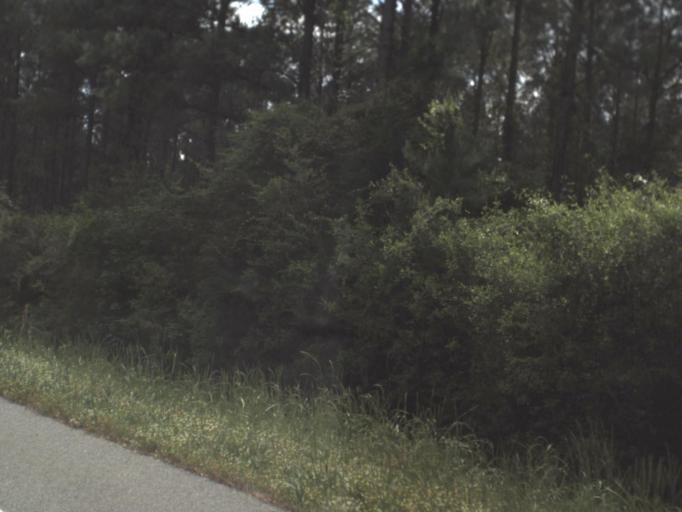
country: US
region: Florida
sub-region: Escambia County
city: Molino
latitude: 30.8226
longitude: -87.4356
